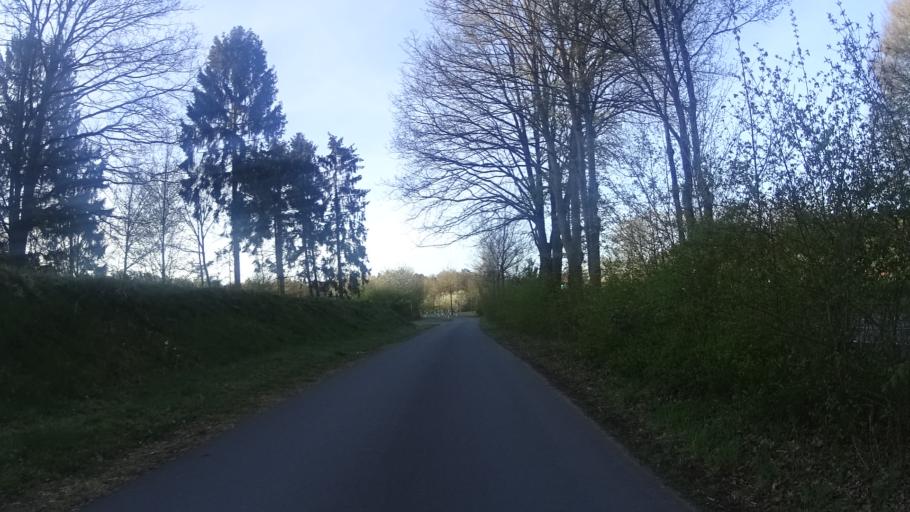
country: DE
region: North Rhine-Westphalia
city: Emsdetten
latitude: 52.2156
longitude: 7.5069
